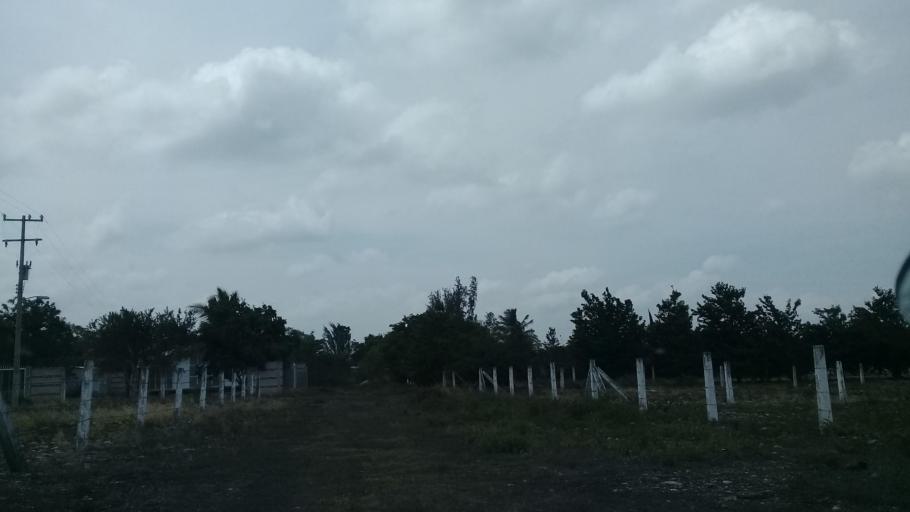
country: MX
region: Veracruz
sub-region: Emiliano Zapata
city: Plan del Rio
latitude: 19.3566
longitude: -96.6577
